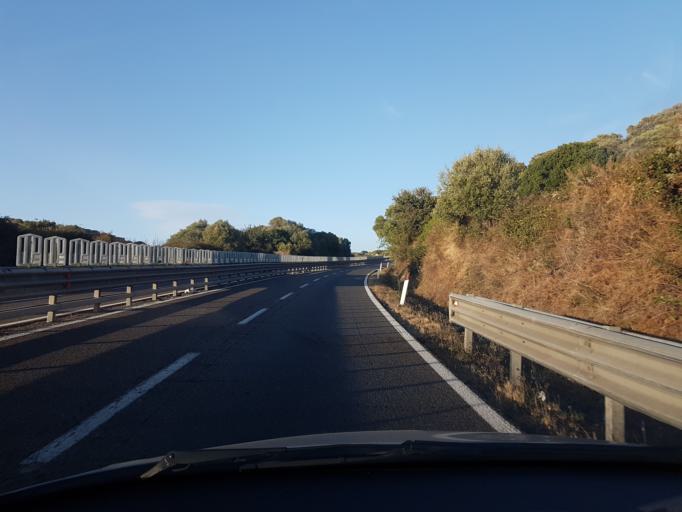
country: IT
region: Sardinia
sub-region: Provincia di Oristano
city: Bauladu
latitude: 40.0519
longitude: 8.7097
